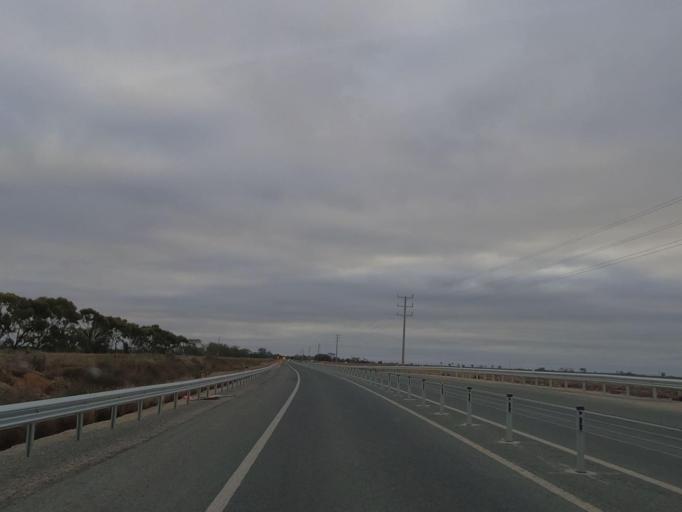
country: AU
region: Victoria
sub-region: Swan Hill
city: Swan Hill
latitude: -35.5436
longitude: 143.7572
